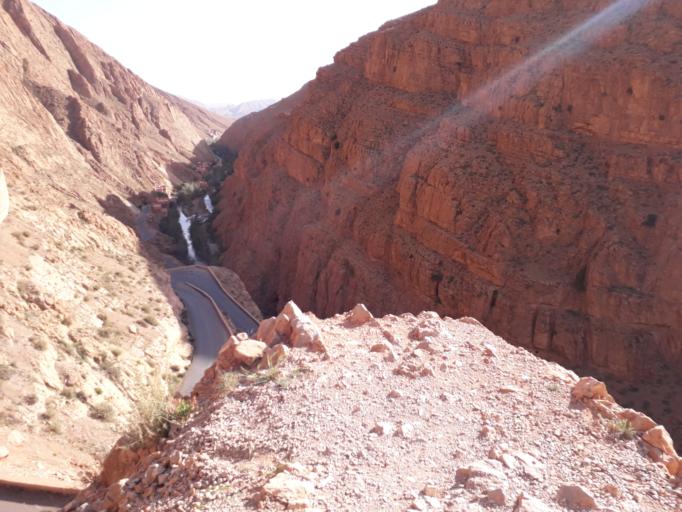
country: MA
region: Souss-Massa-Draa
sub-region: Ouarzazate
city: Imider
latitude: 31.5313
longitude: -5.9235
